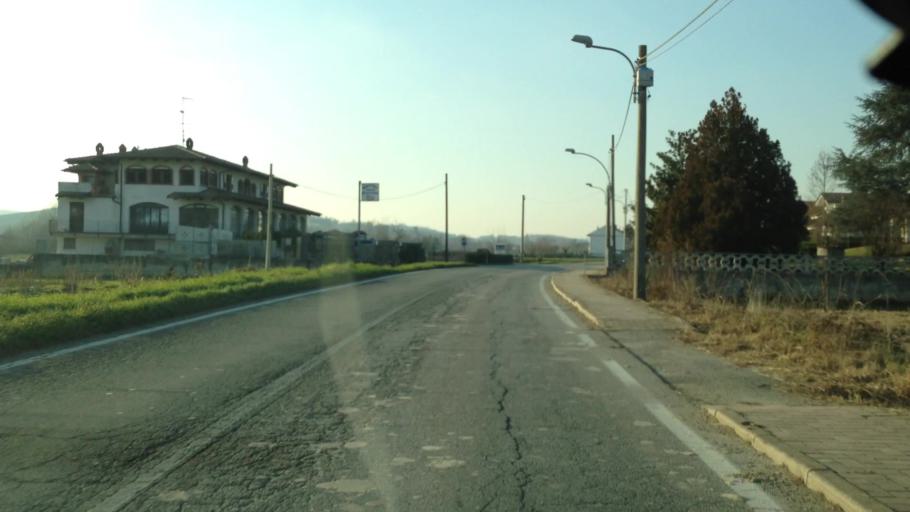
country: IT
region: Piedmont
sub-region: Provincia di Asti
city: Montegrosso
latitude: 44.8166
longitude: 8.2517
